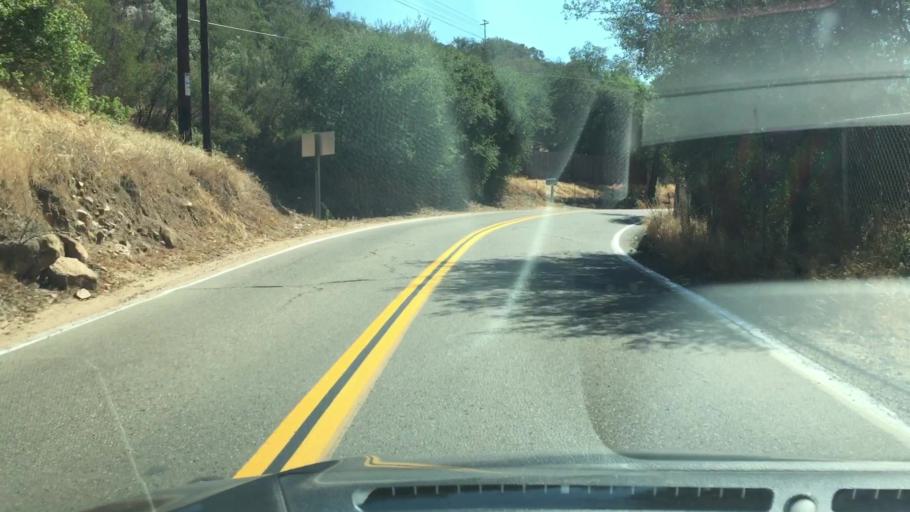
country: US
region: California
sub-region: San Diego County
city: Harbison Canyon
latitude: 32.7519
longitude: -116.7846
